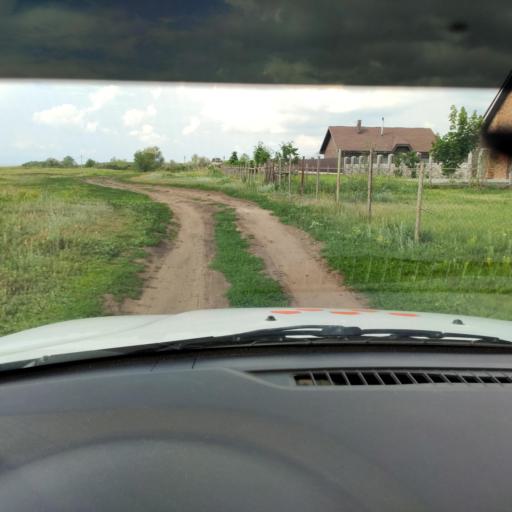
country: RU
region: Samara
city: Podstepki
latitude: 53.6114
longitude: 49.0302
